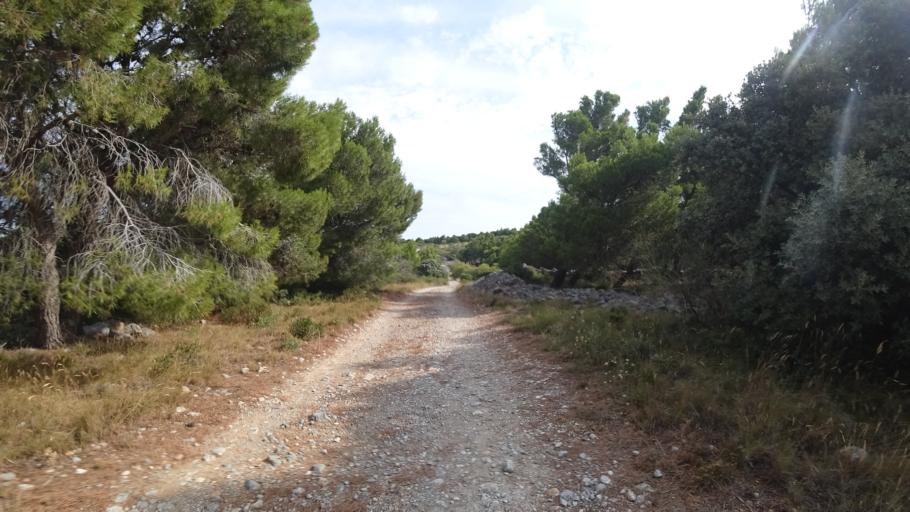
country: FR
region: Languedoc-Roussillon
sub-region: Departement de l'Aude
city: Leucate
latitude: 42.8993
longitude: 3.0242
